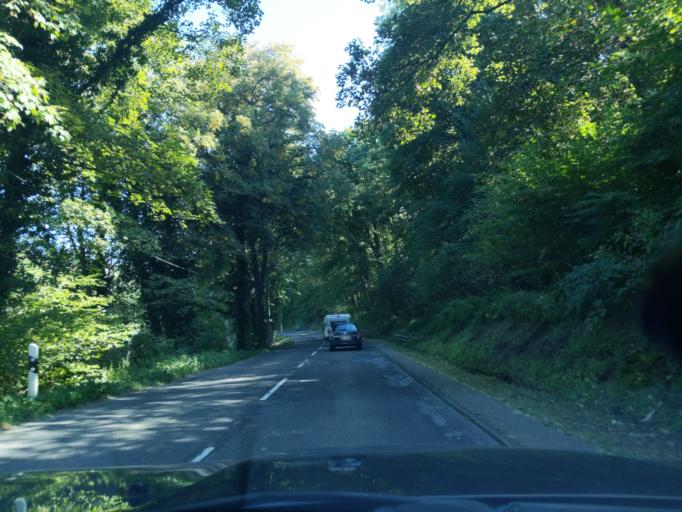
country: DE
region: North Rhine-Westphalia
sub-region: Regierungsbezirk Koln
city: Hennef
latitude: 50.7666
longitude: 7.3496
